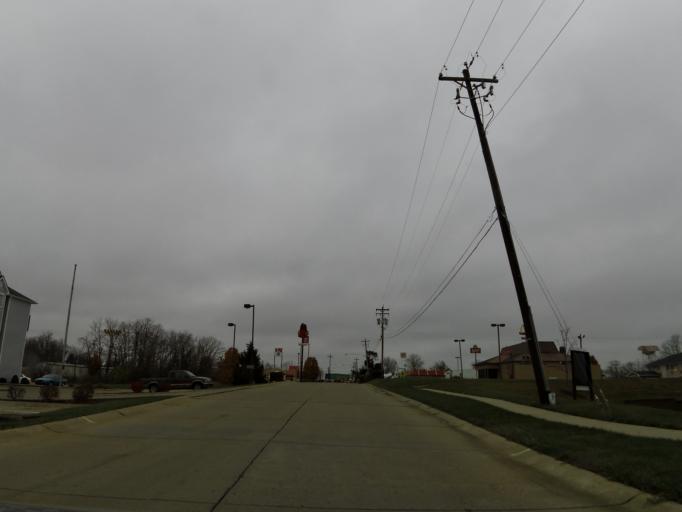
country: US
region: Kentucky
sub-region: Grant County
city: Dry Ridge
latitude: 38.6850
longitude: -84.5995
